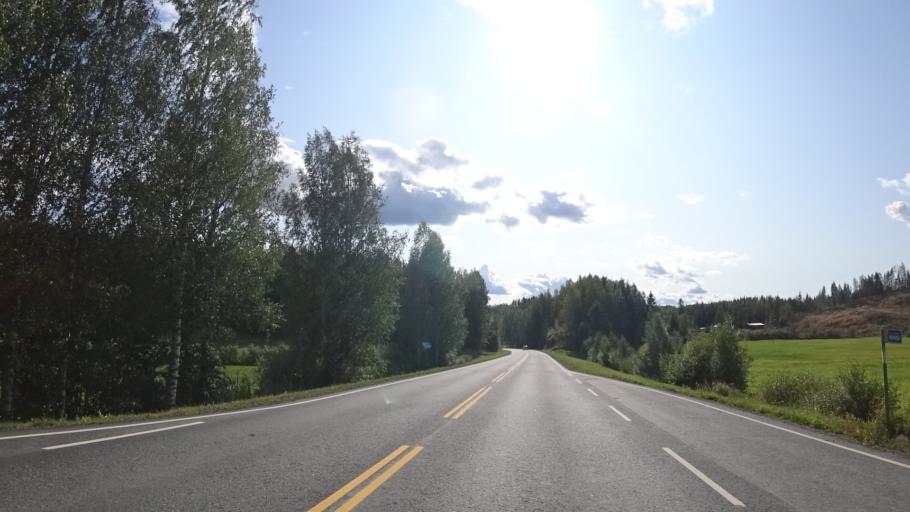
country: FI
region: North Karelia
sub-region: Keski-Karjala
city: Tohmajaervi
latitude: 62.2105
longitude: 30.2889
